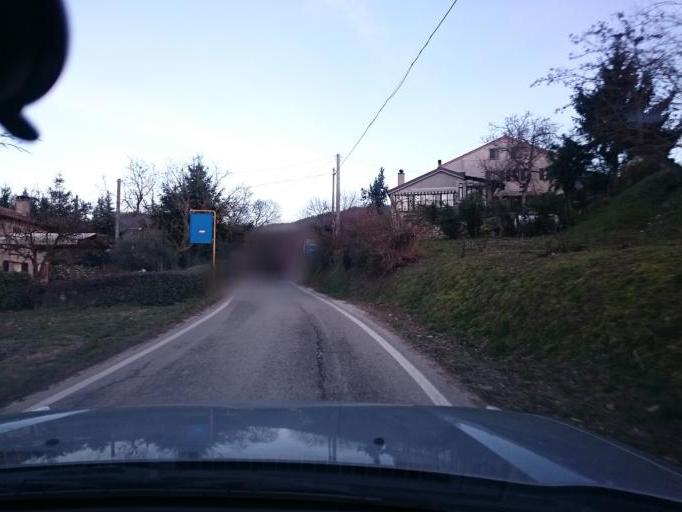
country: IT
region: Veneto
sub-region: Provincia di Padova
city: Vo
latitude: 45.3209
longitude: 11.6649
